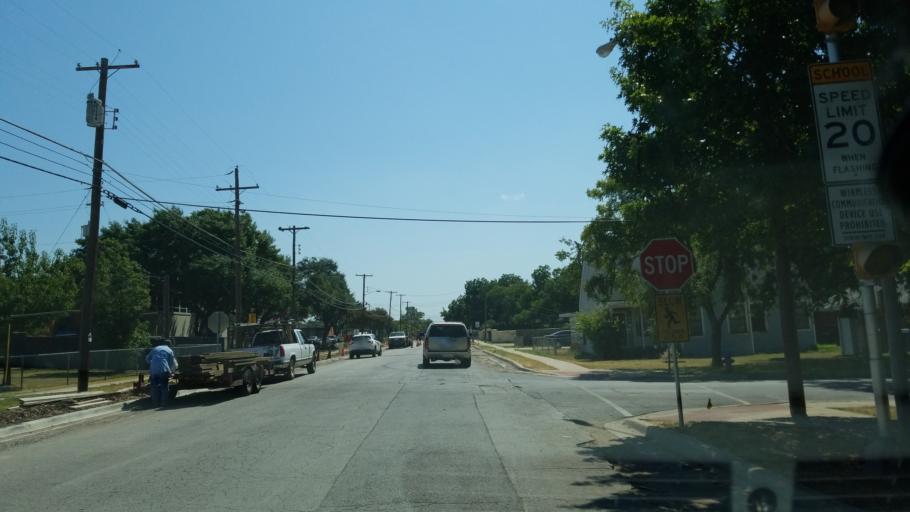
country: US
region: Texas
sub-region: Dallas County
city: Cockrell Hill
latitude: 32.7423
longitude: -96.8860
